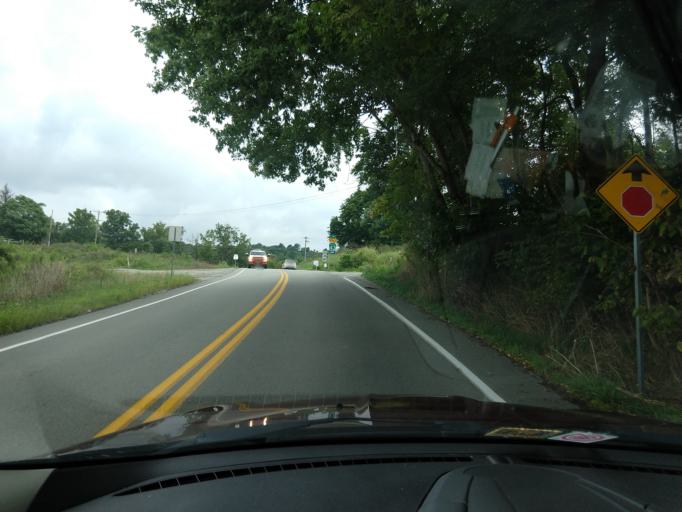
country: US
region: Pennsylvania
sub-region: Washington County
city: Baidland
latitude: 40.1940
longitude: -79.9980
